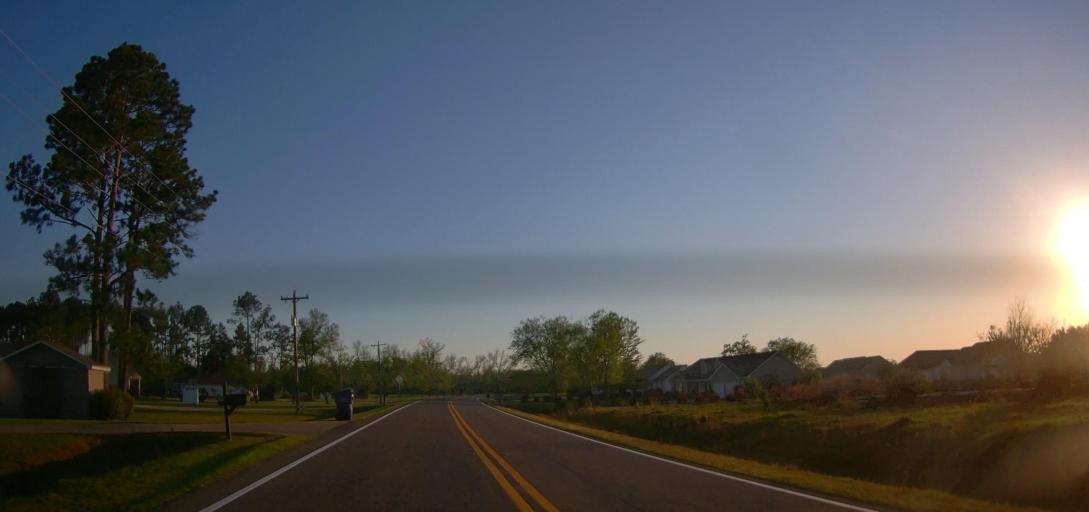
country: US
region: Georgia
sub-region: Irwin County
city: Ocilla
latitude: 31.6431
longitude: -83.2702
